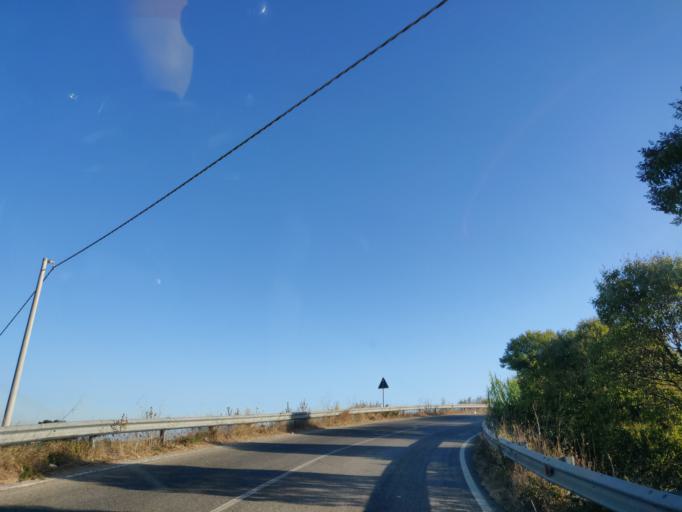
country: IT
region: Latium
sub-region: Provincia di Viterbo
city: Montalto di Castro
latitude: 42.2998
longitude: 11.6503
